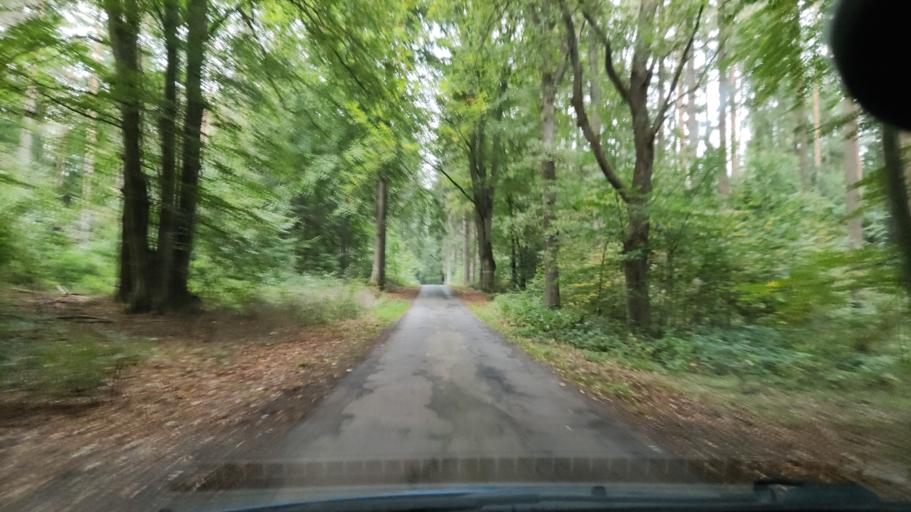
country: DE
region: Lower Saxony
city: Karwitz
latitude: 53.0893
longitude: 10.9775
